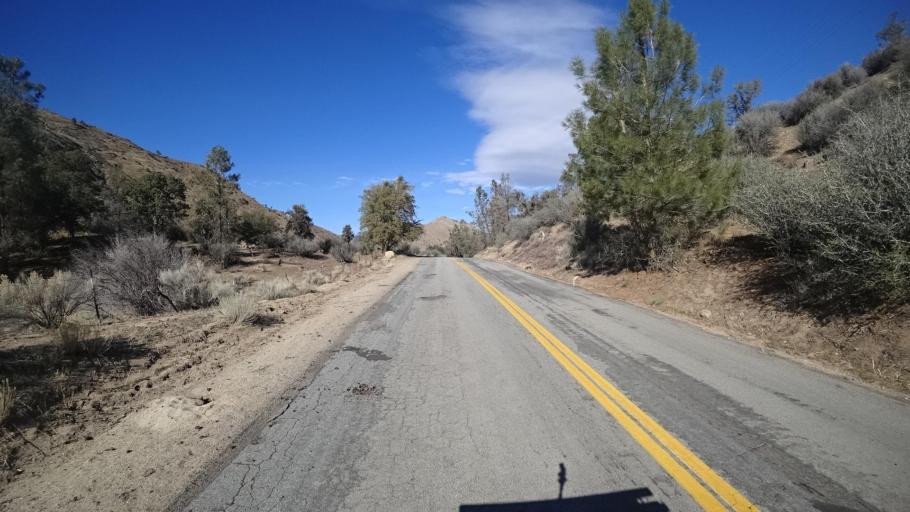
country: US
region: California
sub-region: Kern County
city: Bodfish
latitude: 35.5321
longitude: -118.5121
